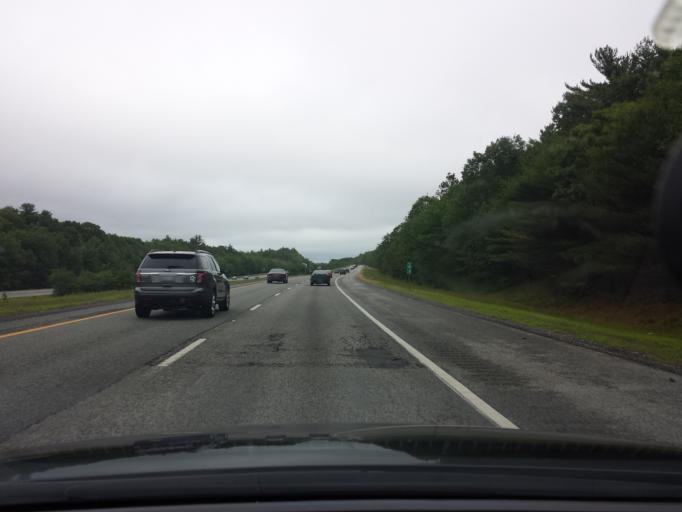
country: US
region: Rhode Island
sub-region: Kent County
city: West Greenwich
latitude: 41.6144
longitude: -71.6510
